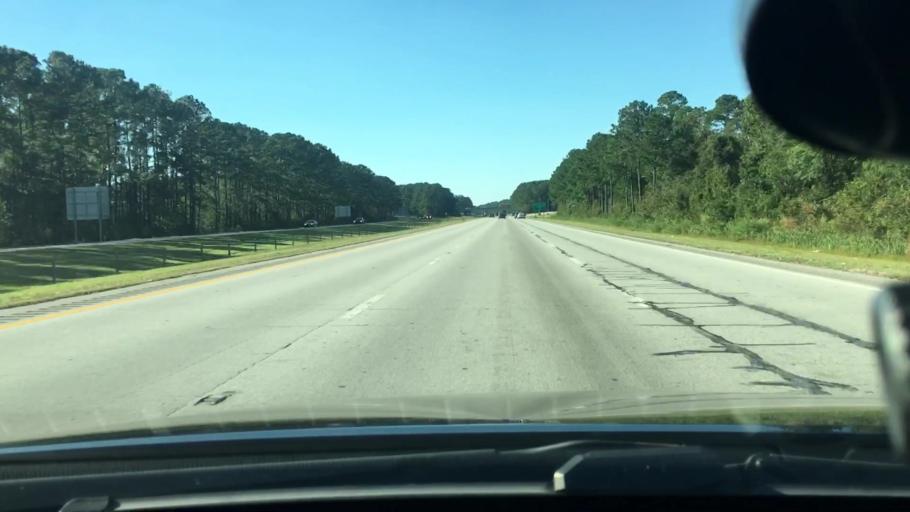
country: US
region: North Carolina
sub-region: Craven County
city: Trent Woods
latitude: 35.1079
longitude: -77.0901
